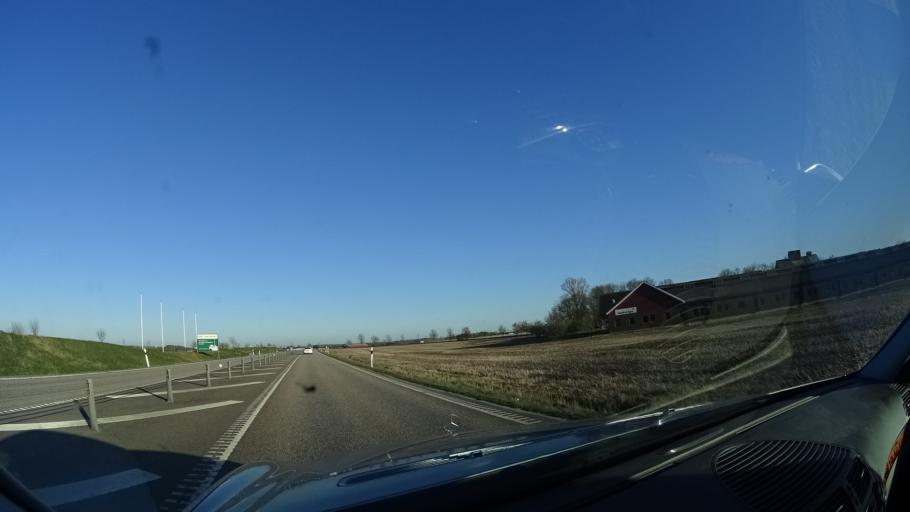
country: SE
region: Skane
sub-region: Helsingborg
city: Hyllinge
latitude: 56.0920
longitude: 12.8674
